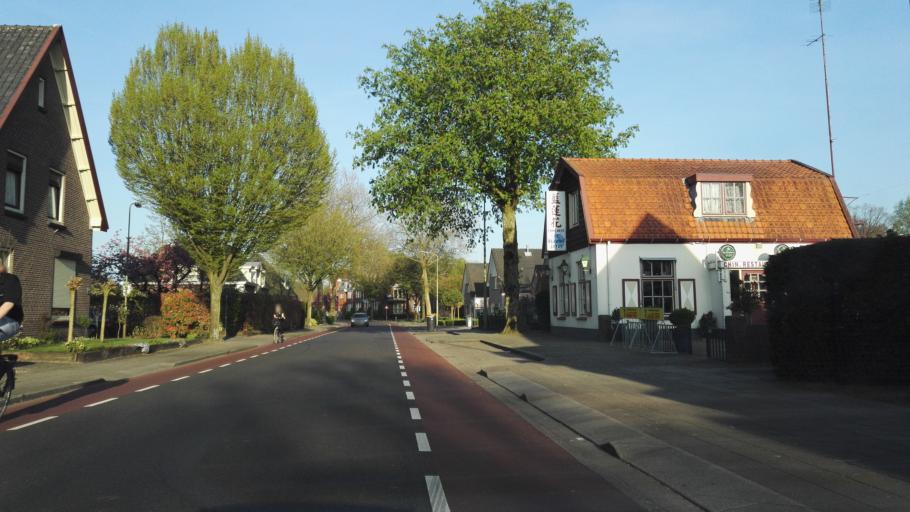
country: NL
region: Gelderland
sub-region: Gemeente Epe
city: Vaassen
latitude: 52.2901
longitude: 5.9711
